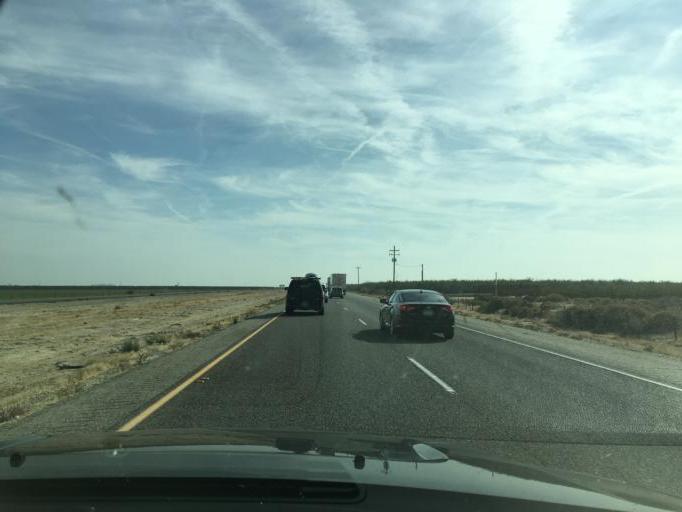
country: US
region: California
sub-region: Kern County
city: Buttonwillow
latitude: 35.4688
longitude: -119.4936
